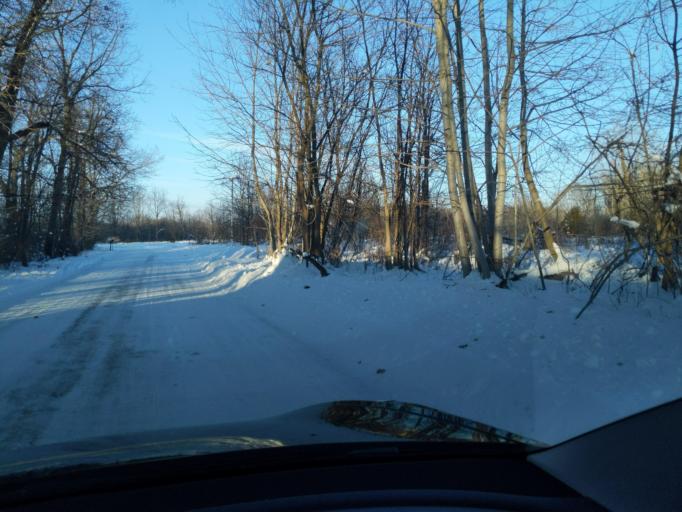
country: US
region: Michigan
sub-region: Ingham County
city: Stockbridge
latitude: 42.4889
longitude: -84.1191
